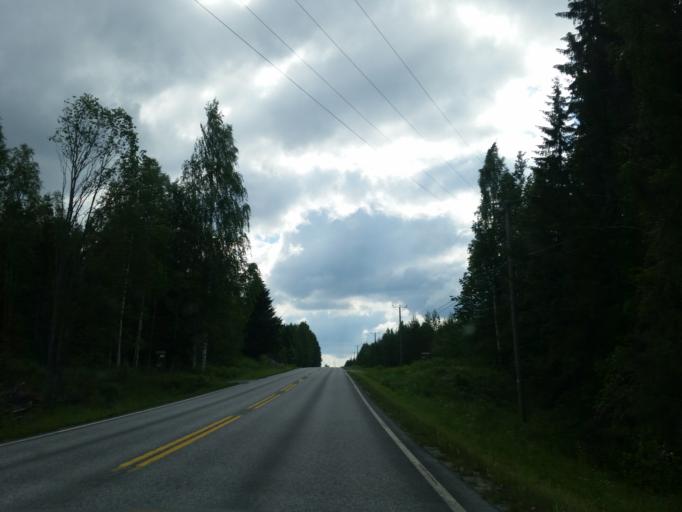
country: FI
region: Northern Savo
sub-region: Kuopio
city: Kuopio
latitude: 62.8448
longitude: 27.4657
